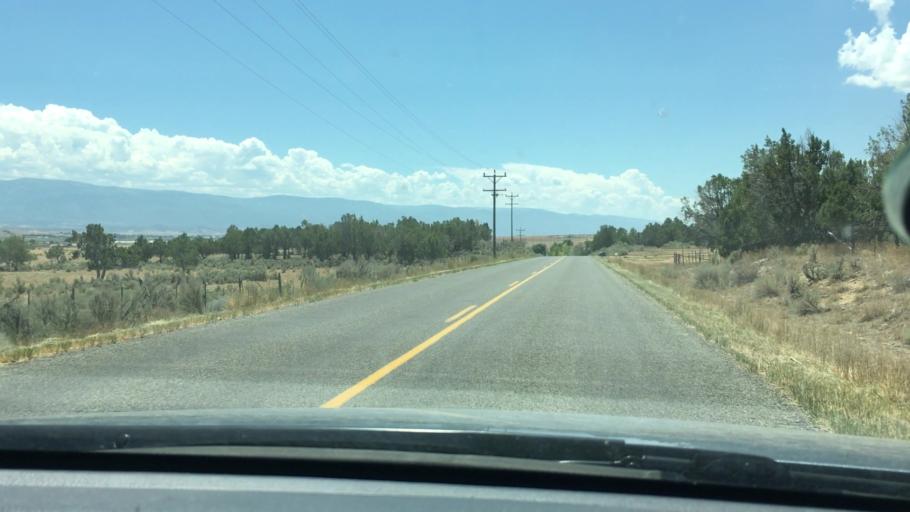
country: US
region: Utah
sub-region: Sanpete County
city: Fountain Green
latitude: 39.5916
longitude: -111.6426
